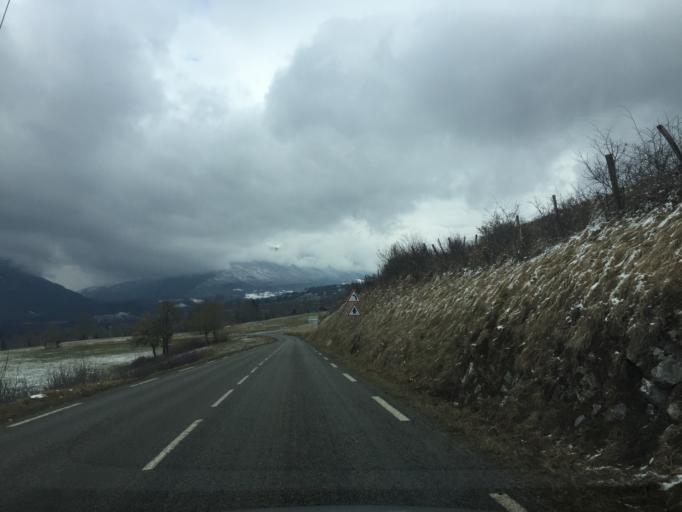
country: FR
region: Rhone-Alpes
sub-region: Departement de la Haute-Savoie
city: Gruffy
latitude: 45.6935
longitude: 6.1275
